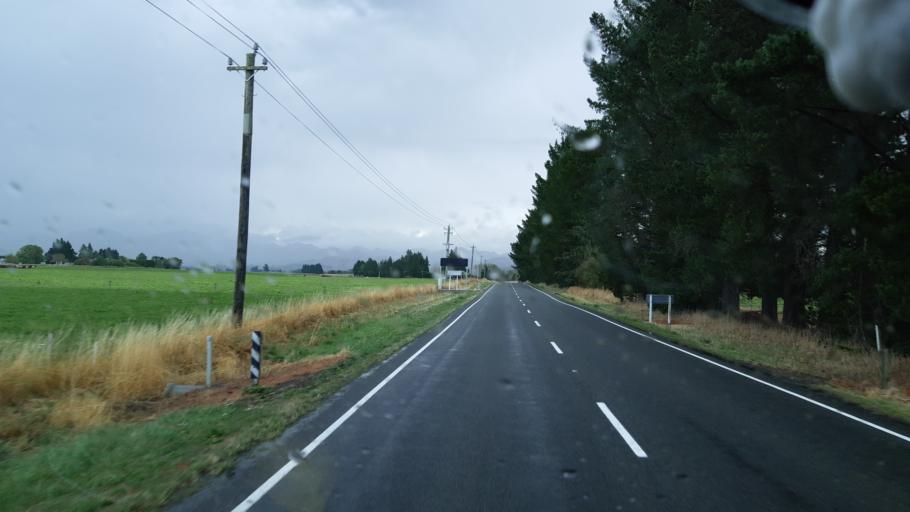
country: NZ
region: Canterbury
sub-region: Hurunui District
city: Amberley
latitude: -42.7155
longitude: 172.8652
